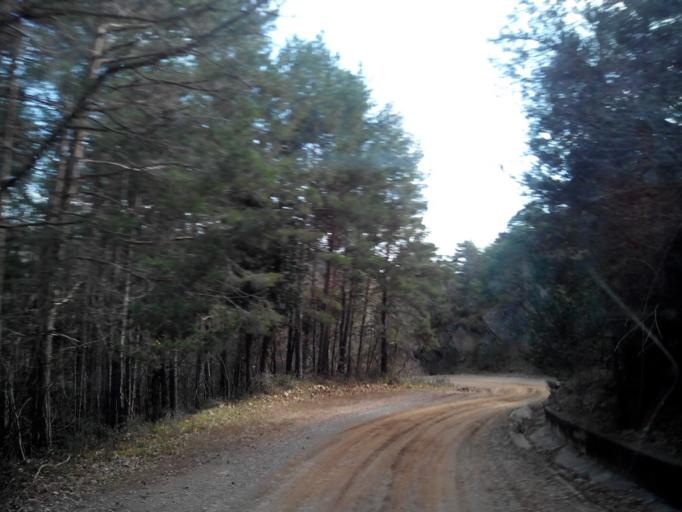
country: ES
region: Catalonia
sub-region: Provincia de Barcelona
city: Vilada
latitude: 42.1598
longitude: 1.9273
